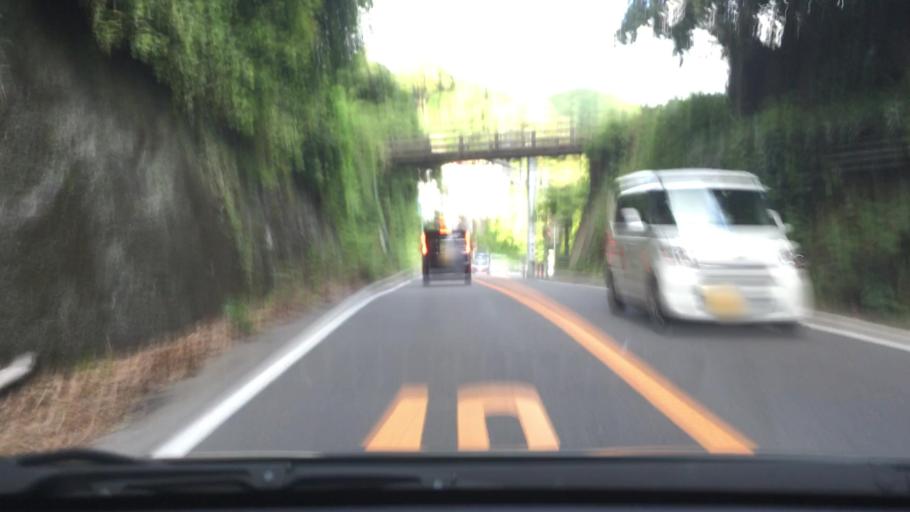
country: JP
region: Nagasaki
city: Togitsu
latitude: 32.8084
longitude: 129.8143
